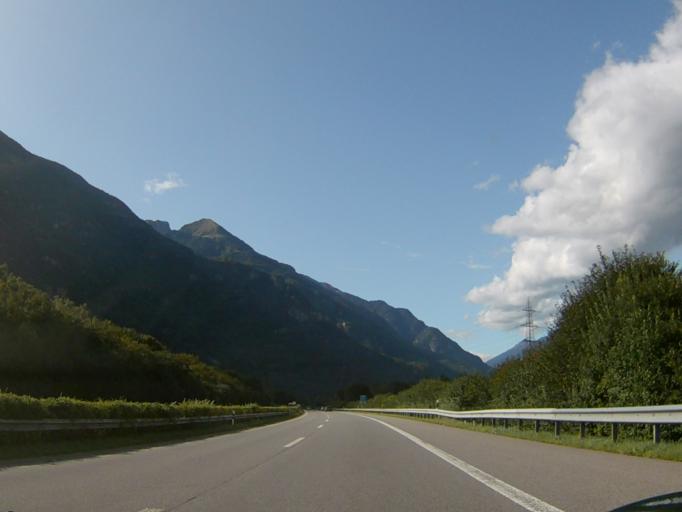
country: CH
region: Ticino
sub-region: Riviera District
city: Claro
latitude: 46.2662
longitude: 9.0058
